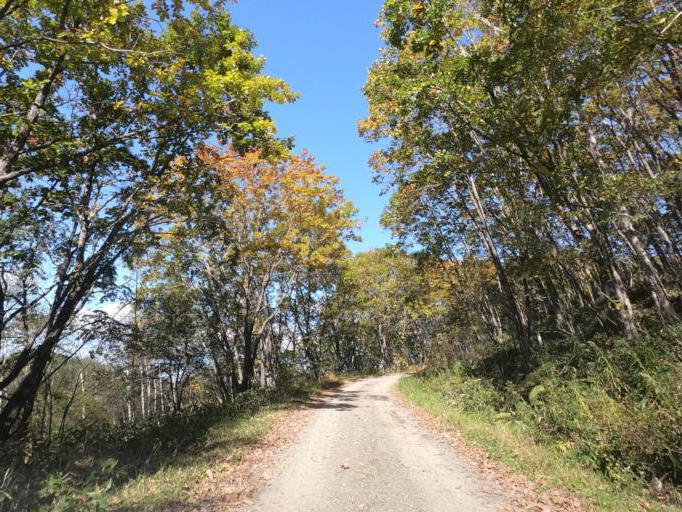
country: JP
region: Hokkaido
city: Obihiro
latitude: 42.7269
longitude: 143.4500
